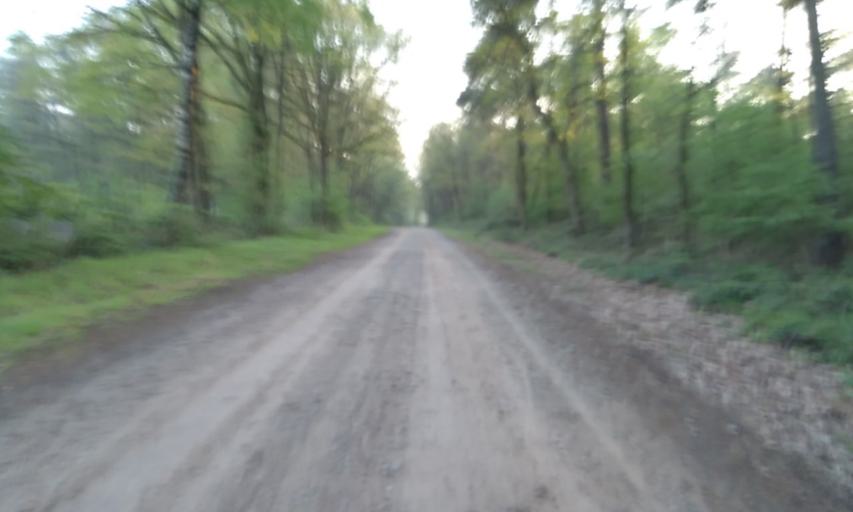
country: DE
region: Lower Saxony
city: Bargstedt
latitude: 53.5000
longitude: 9.4439
